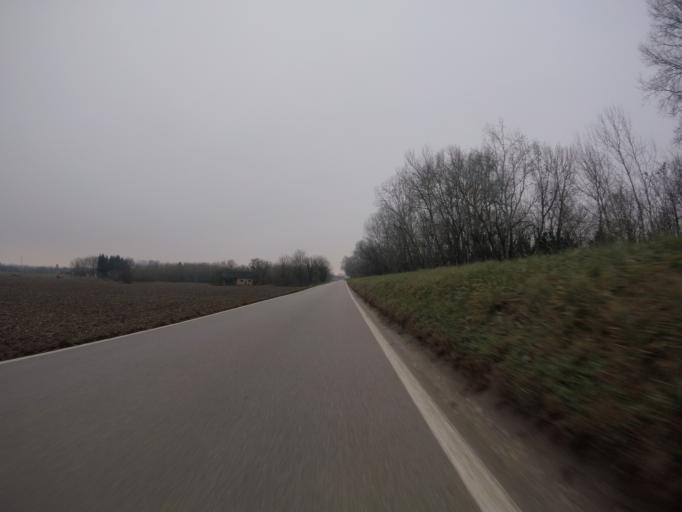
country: HR
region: Zagrebacka
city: Kuce
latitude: 45.6888
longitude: 16.2407
